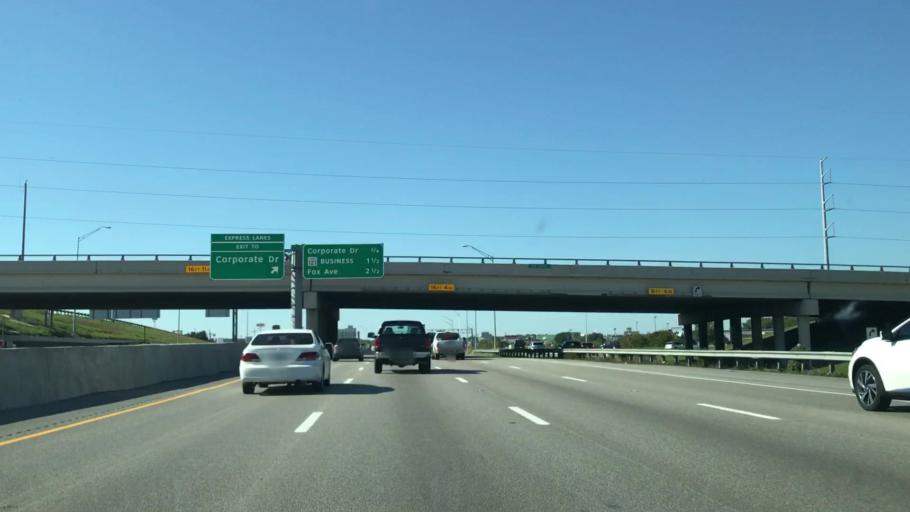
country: US
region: Texas
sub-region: Denton County
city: Lewisville
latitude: 33.0066
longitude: -96.9714
